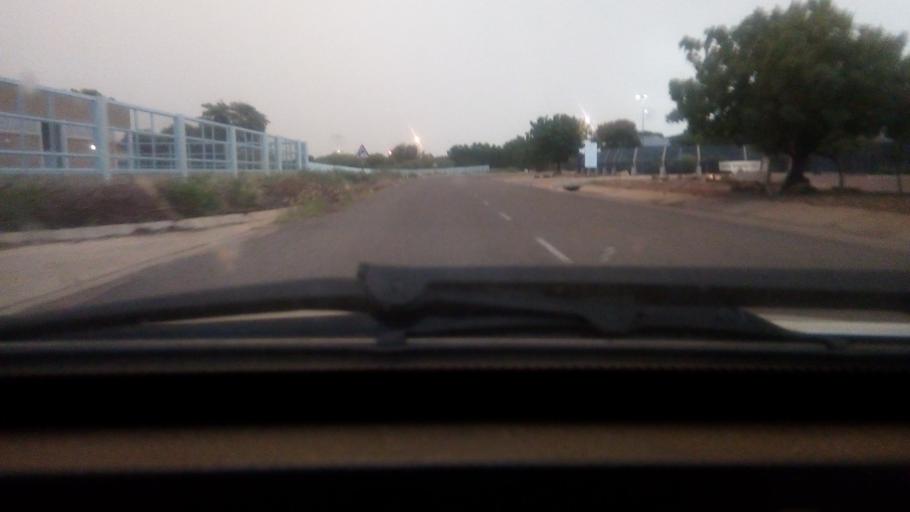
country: BW
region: Kweneng
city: Mmopone
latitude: -24.5907
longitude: 25.9159
